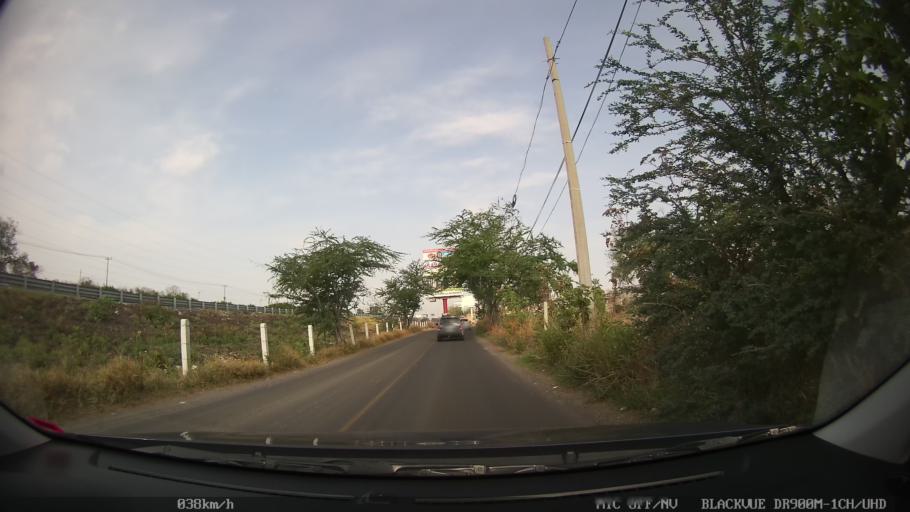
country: MX
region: Jalisco
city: Tonala
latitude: 20.6182
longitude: -103.2249
